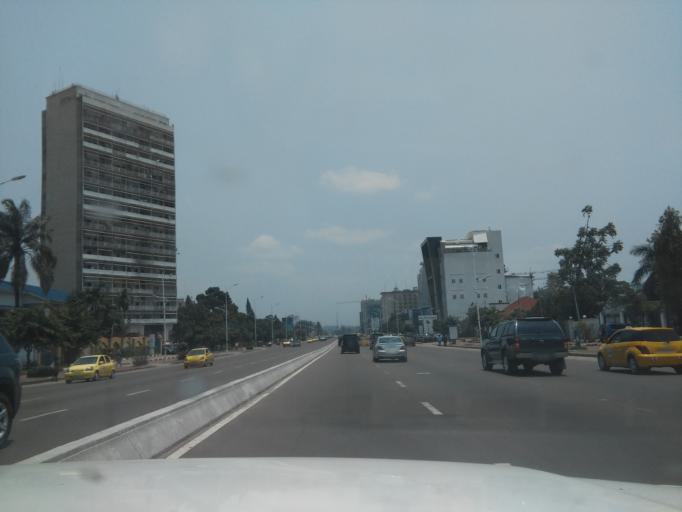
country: CD
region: Kinshasa
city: Kinshasa
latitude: -4.3121
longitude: 15.2866
